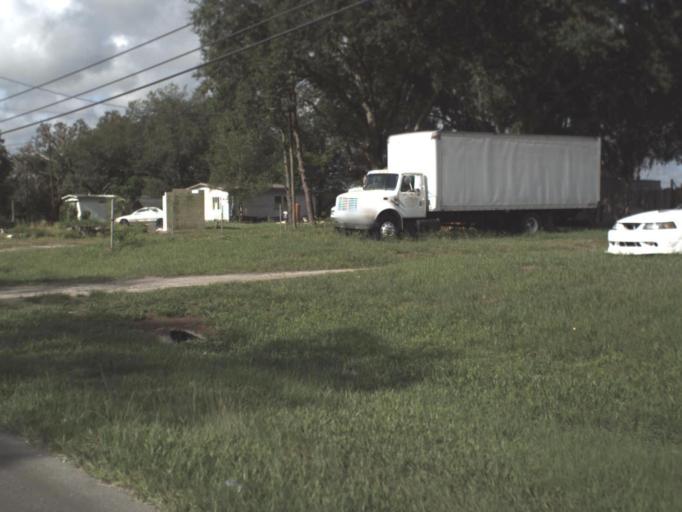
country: US
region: Florida
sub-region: Pasco County
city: Shady Hills
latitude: 28.3382
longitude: -82.5013
